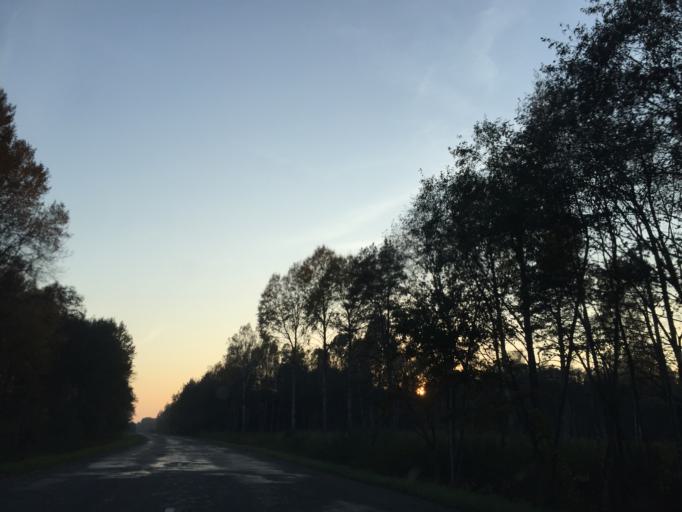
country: LT
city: Skuodas
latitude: 56.3464
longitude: 21.5845
